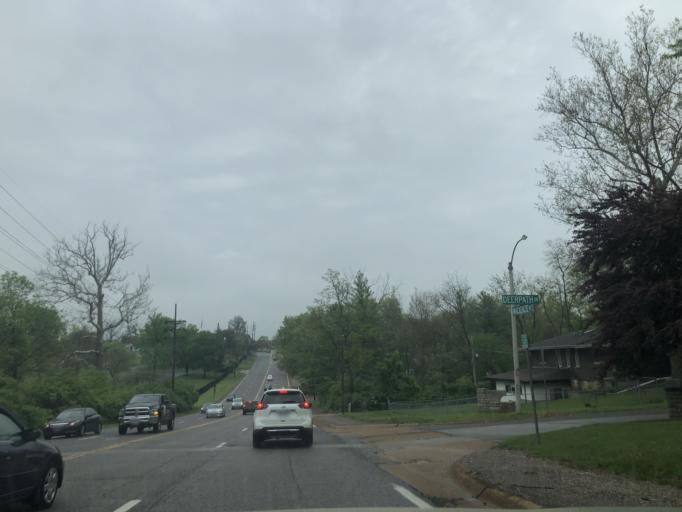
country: US
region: Missouri
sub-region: Saint Louis County
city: Marlborough
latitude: 38.5795
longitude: -90.3185
